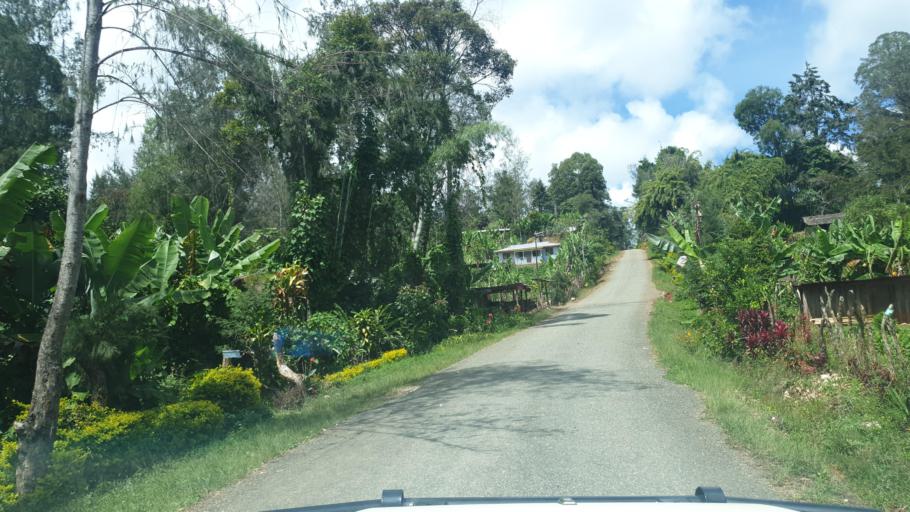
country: PG
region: Chimbu
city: Kundiawa
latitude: -6.1570
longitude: 145.1346
